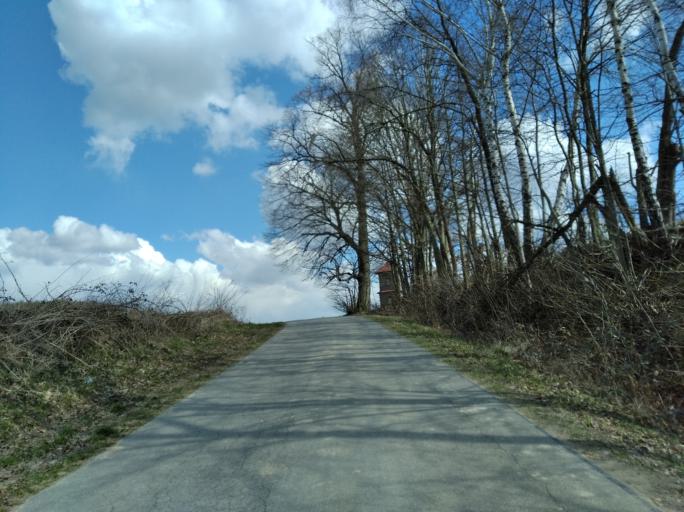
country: PL
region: Subcarpathian Voivodeship
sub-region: Powiat strzyzowski
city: Wisniowa
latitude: 49.9255
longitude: 21.7035
